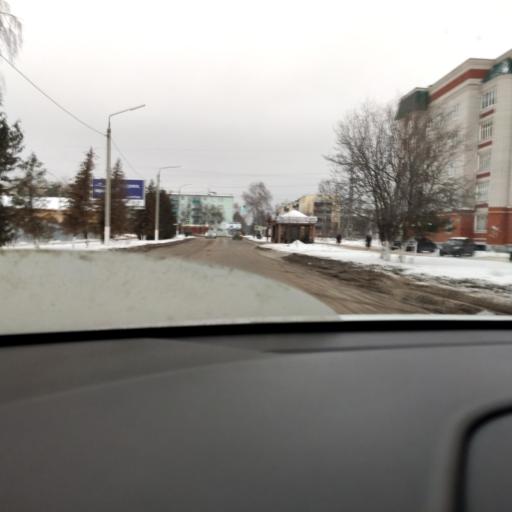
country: RU
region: Tatarstan
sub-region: Zelenodol'skiy Rayon
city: Zelenodolsk
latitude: 55.8520
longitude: 48.5022
